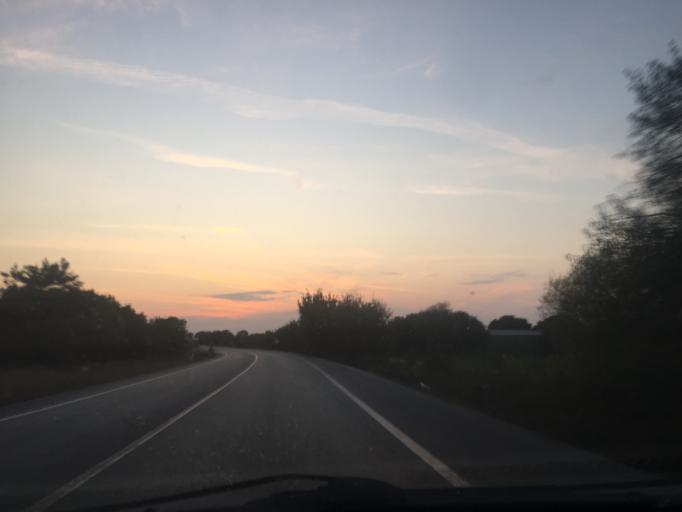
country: TR
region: Canakkale
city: Bayramic
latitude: 39.8102
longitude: 26.5599
